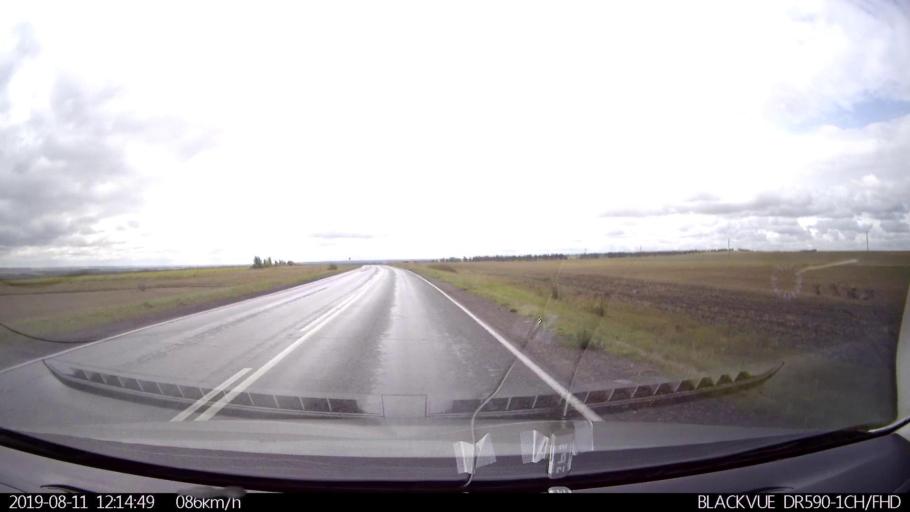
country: RU
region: Ulyanovsk
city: Ignatovka
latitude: 53.9484
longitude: 47.9749
